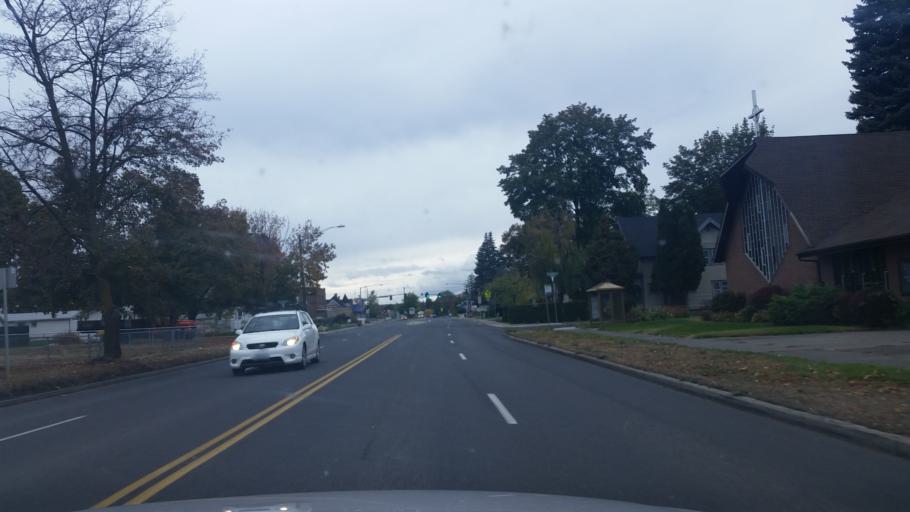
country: US
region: Washington
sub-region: Spokane County
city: Spokane
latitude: 47.6719
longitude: -117.3786
